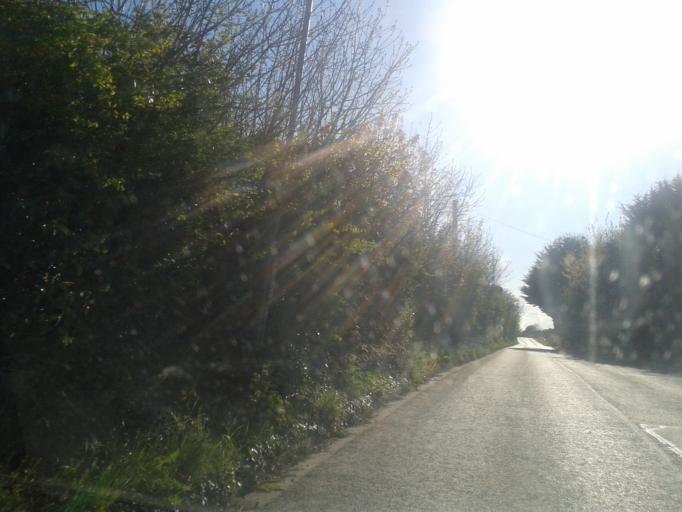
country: IE
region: Leinster
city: Kinsealy-Drinan
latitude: 53.4409
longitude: -6.2023
